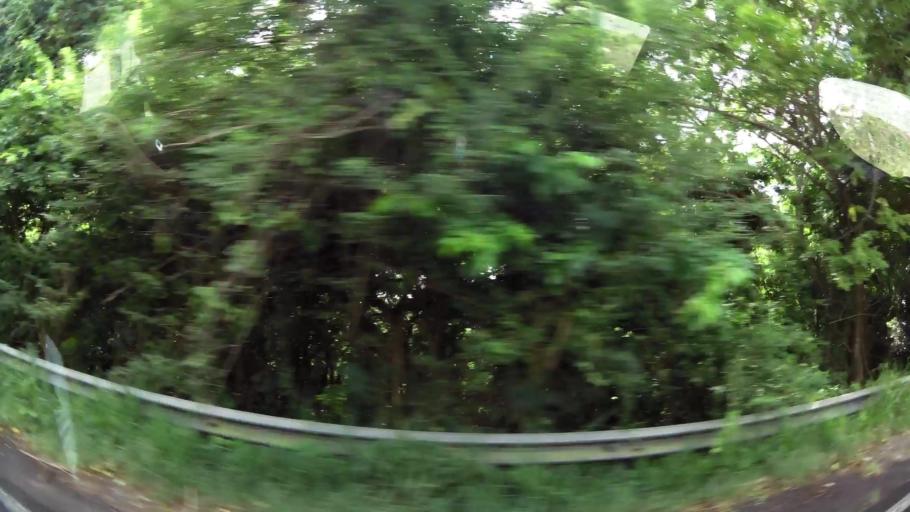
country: MQ
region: Martinique
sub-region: Martinique
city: Les Trois-Ilets
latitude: 14.4816
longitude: -61.0095
